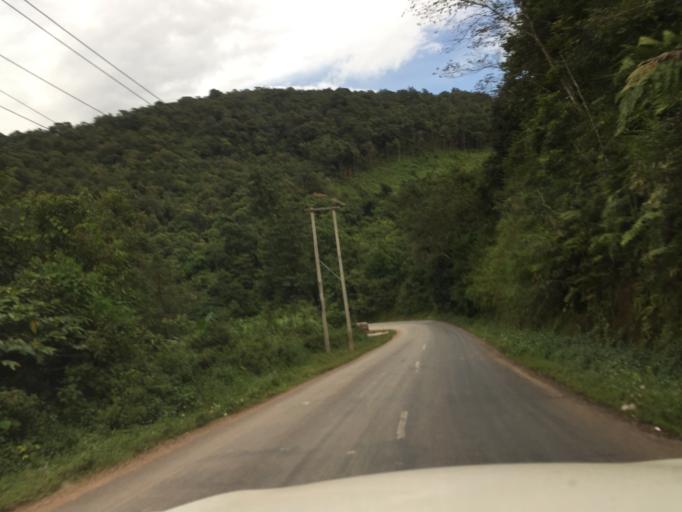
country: LA
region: Phongsali
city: Phongsali
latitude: 21.3283
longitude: 102.0520
